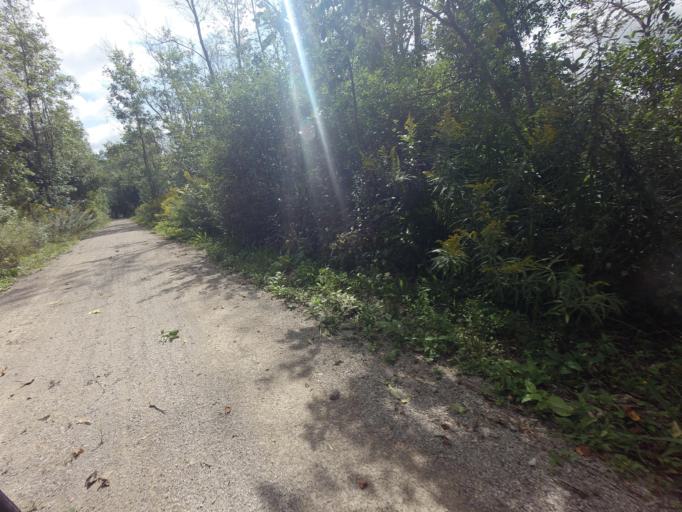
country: CA
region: Ontario
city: Huron East
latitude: 43.6189
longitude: -81.1509
